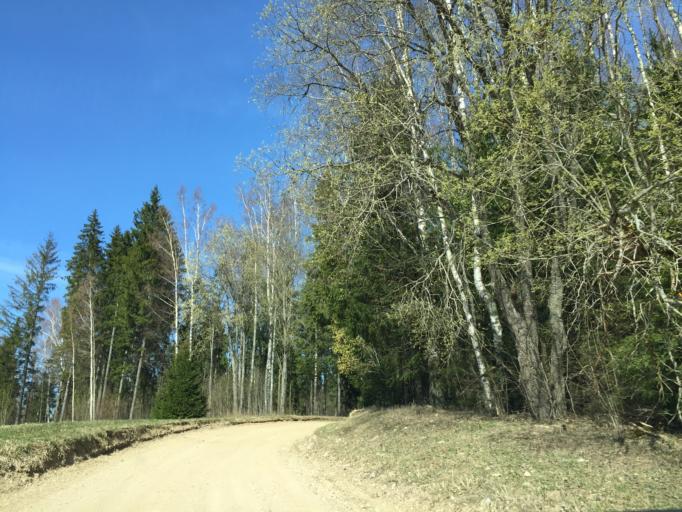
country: EE
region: Vorumaa
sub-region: Antsla vald
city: Vana-Antsla
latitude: 57.9796
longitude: 26.3537
